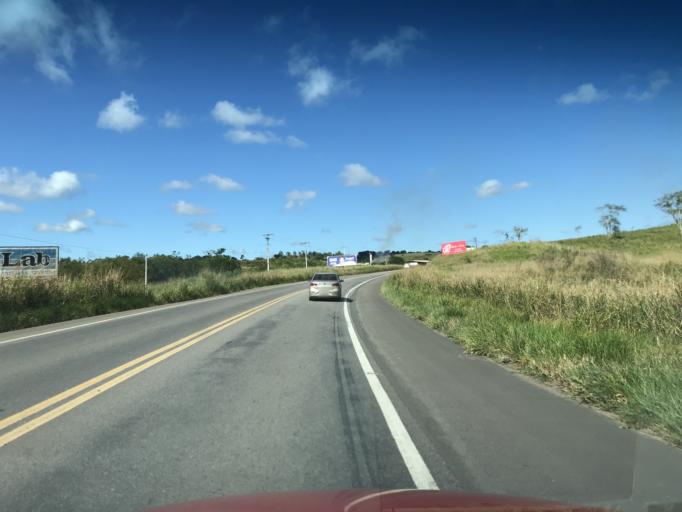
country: BR
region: Bahia
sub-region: Conceicao Do Almeida
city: Muritiba
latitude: -12.9405
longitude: -39.2513
